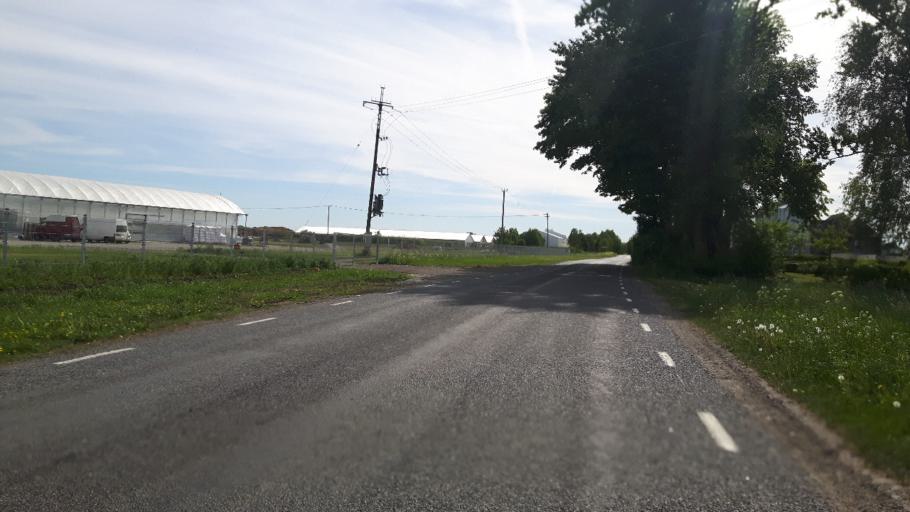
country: EE
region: Harju
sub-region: Raasiku vald
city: Arukula
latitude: 59.4297
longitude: 25.1111
